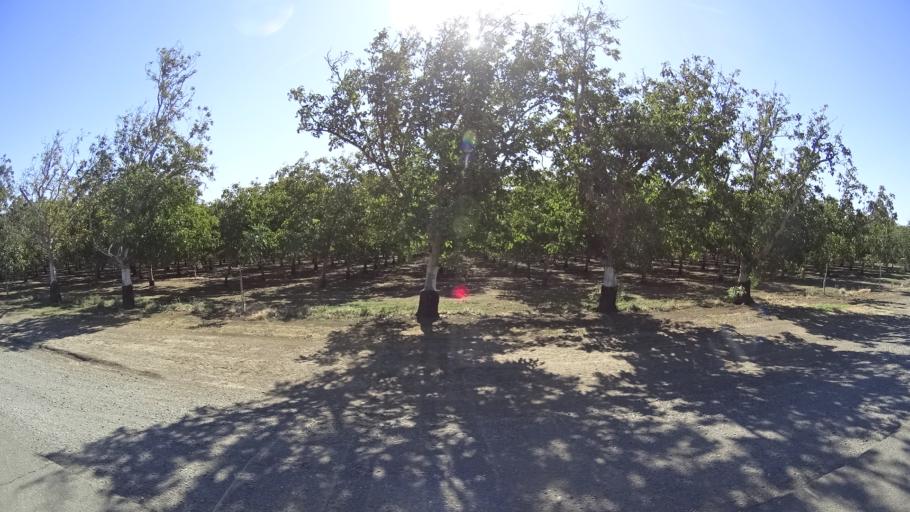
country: US
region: California
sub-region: Yolo County
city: Winters
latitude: 38.5452
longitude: -121.9148
